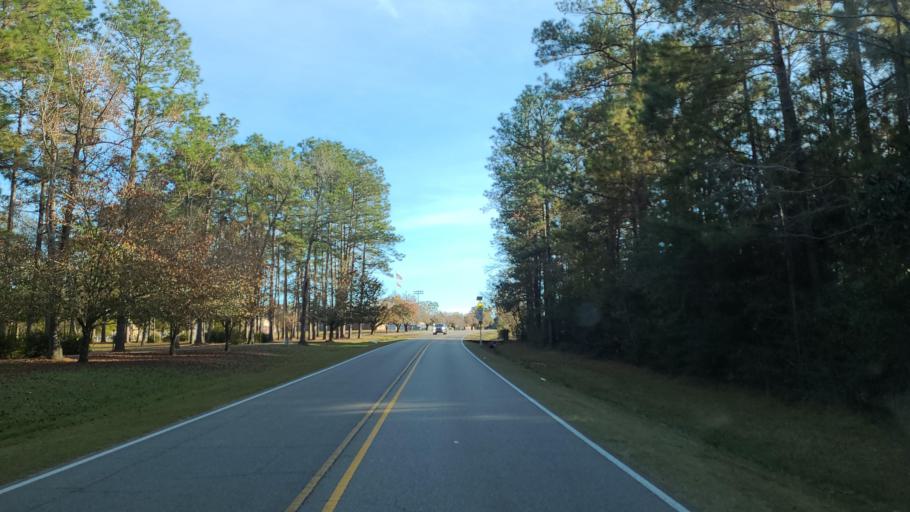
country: US
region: Mississippi
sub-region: Forrest County
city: Hattiesburg
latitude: 31.2197
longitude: -89.3042
